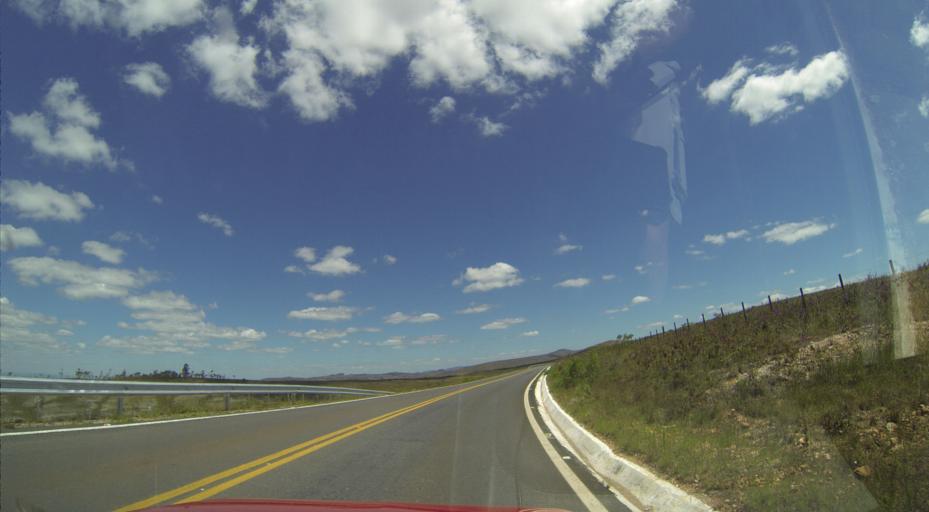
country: BR
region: Minas Gerais
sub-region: Conceicao Do Mato Dentro
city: Conceicao do Mato Dentro
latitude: -19.2531
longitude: -43.5393
